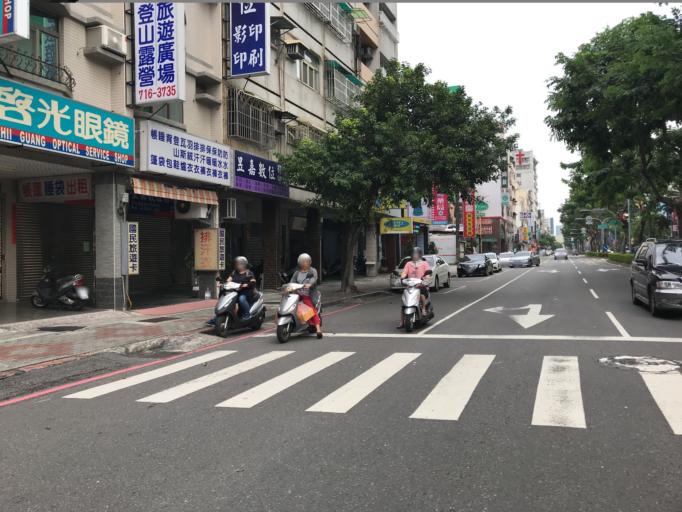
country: TW
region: Kaohsiung
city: Kaohsiung
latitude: 22.6241
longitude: 120.3154
